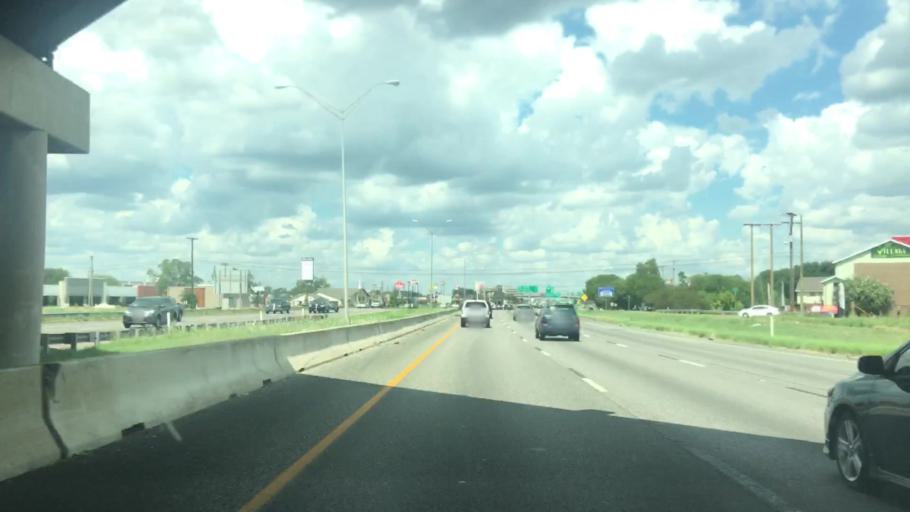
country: US
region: Texas
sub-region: McLennan County
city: Waco
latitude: 31.5425
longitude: -97.1273
